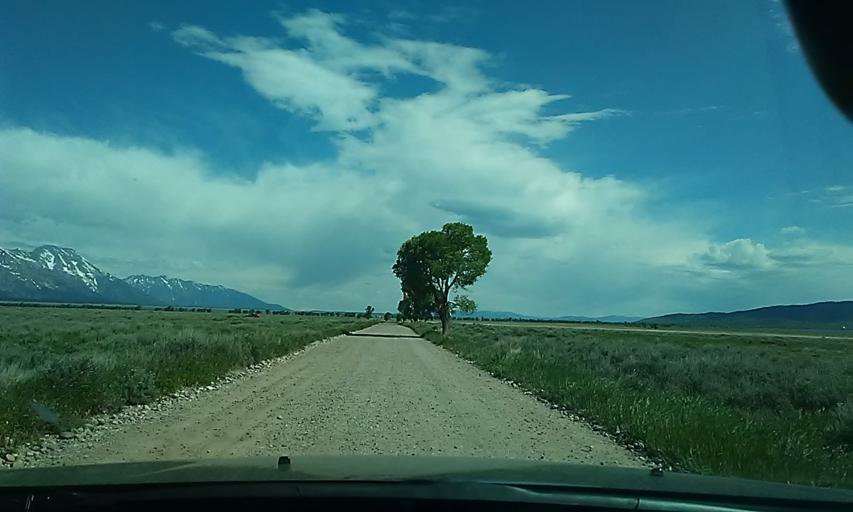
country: US
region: Wyoming
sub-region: Teton County
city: Jackson
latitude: 43.6288
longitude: -110.6642
